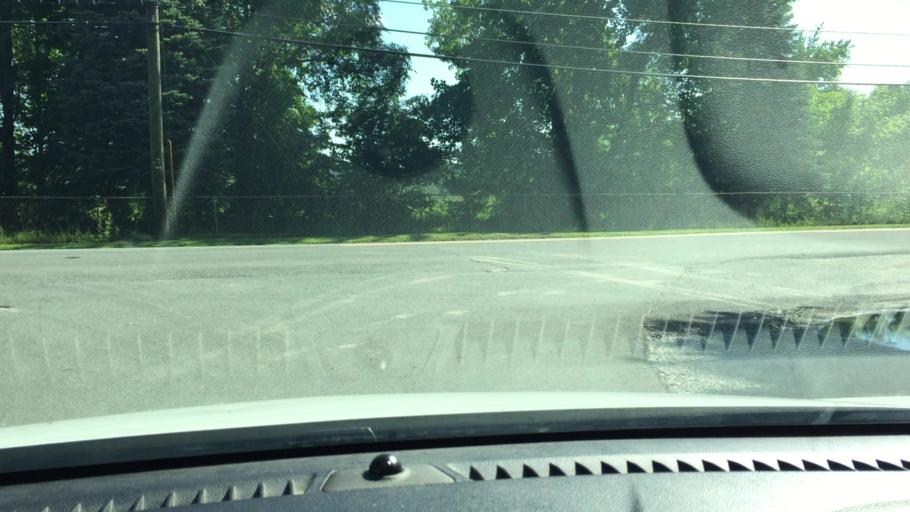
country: US
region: Massachusetts
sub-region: Berkshire County
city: Lanesborough
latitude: 42.5045
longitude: -73.2420
